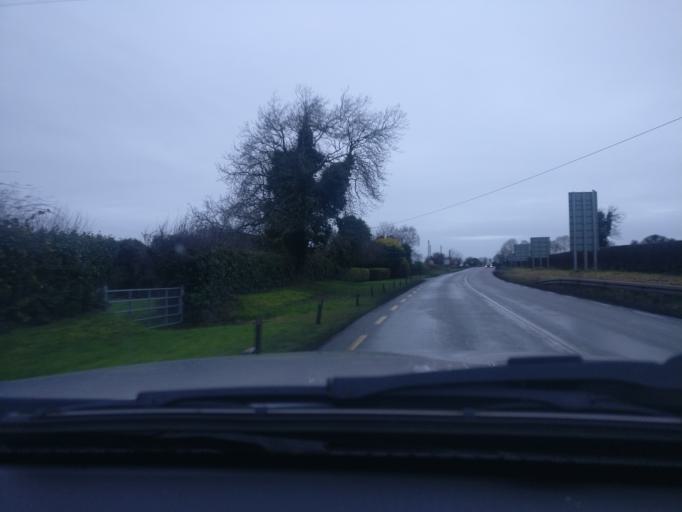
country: IE
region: Leinster
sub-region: An Mhi
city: Dunshaughlin
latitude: 53.5010
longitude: -6.5950
